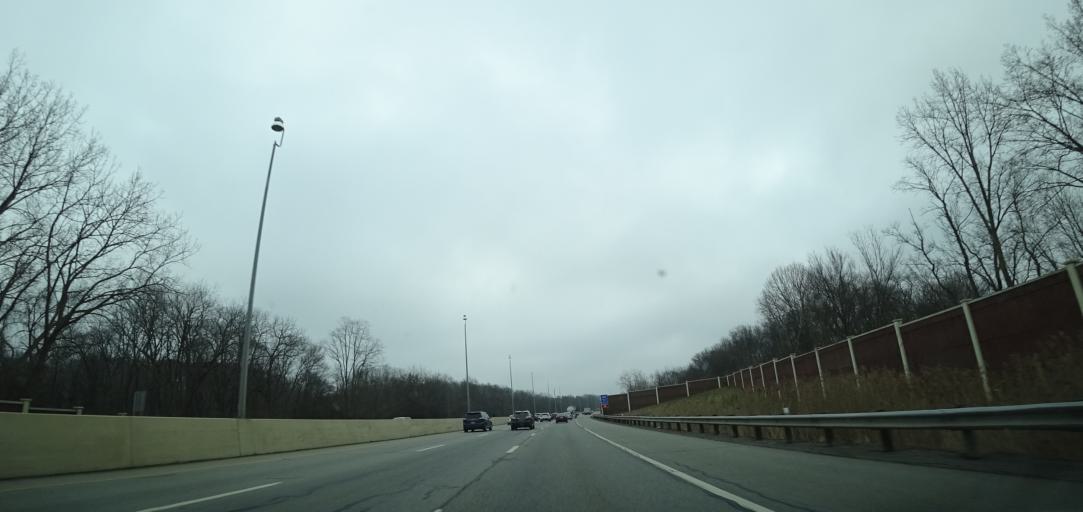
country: US
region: Ohio
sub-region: Summit County
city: Fairlawn
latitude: 41.1182
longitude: -81.6203
